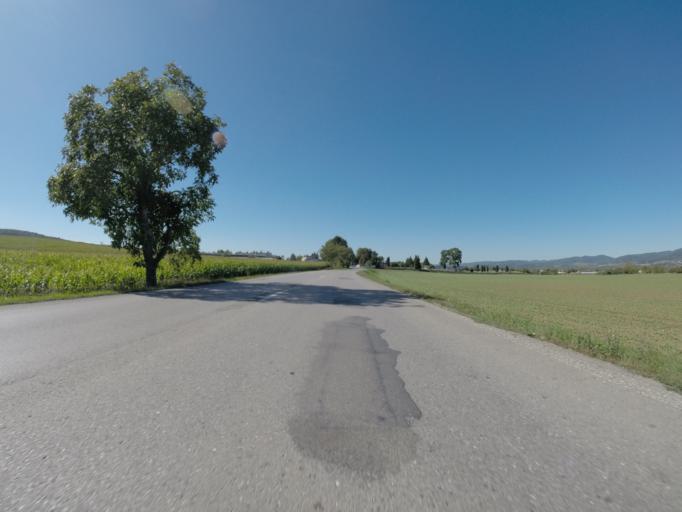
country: SK
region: Nitriansky
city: Ilava
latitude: 49.0023
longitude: 18.2445
